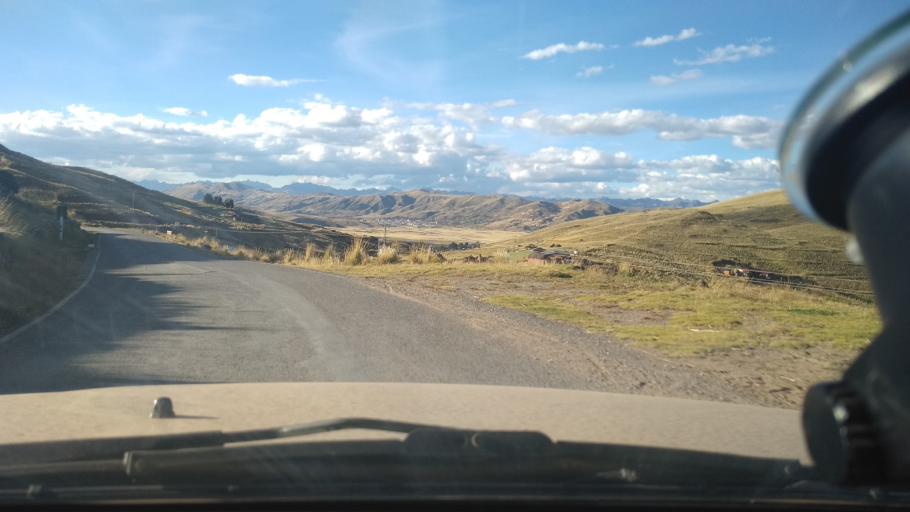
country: PE
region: Cusco
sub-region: Provincia de Canas
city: Ccaquiracunca
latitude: -14.2787
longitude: -71.4485
